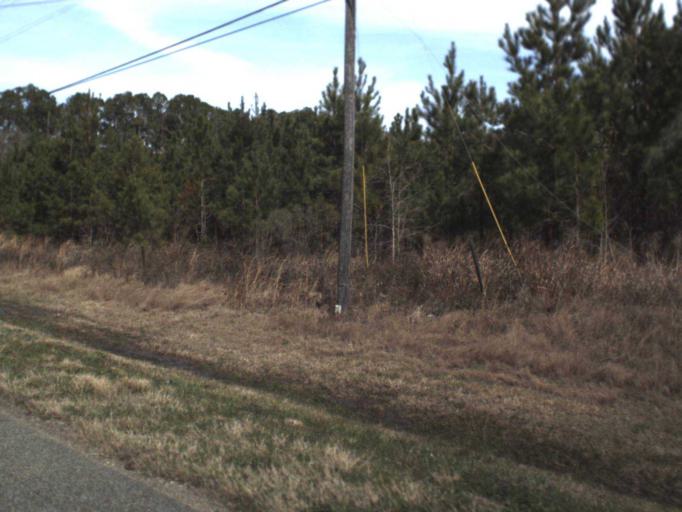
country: US
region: Florida
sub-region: Jackson County
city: Graceville
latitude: 30.9186
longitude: -85.5205
